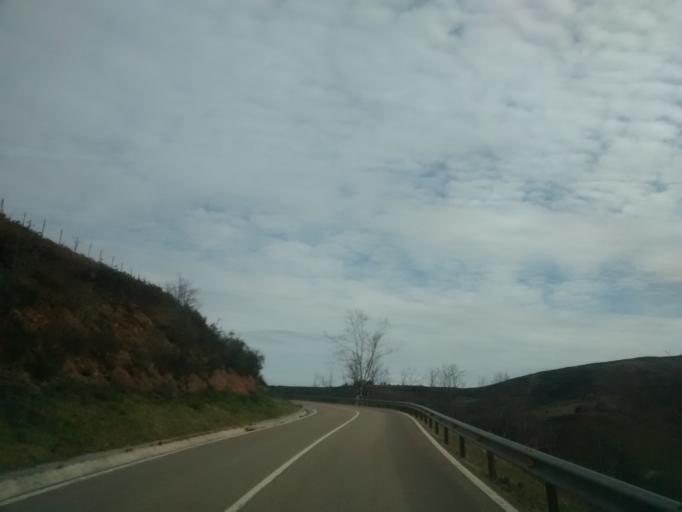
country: ES
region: Cantabria
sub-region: Provincia de Cantabria
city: Ruente
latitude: 43.2488
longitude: -4.3474
